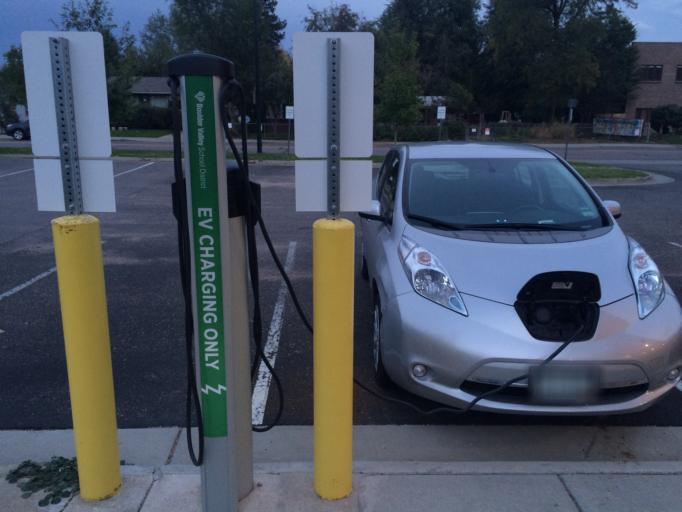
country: US
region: Colorado
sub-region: Boulder County
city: Louisville
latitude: 39.9842
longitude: -105.1326
